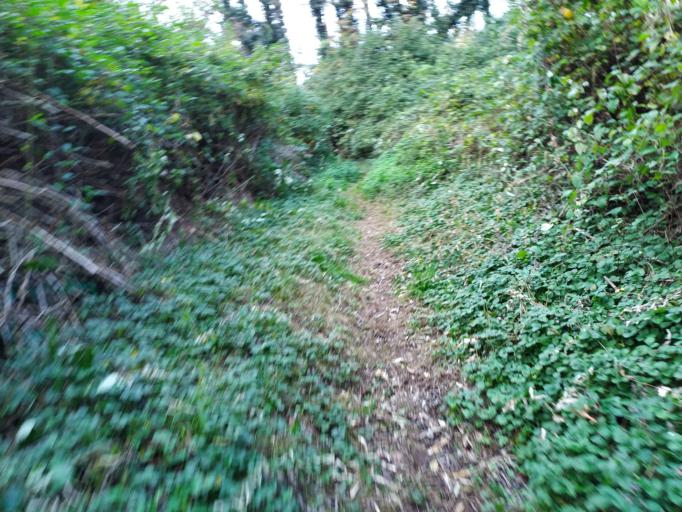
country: IT
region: Veneto
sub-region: Provincia di Vicenza
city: Monte di Malo
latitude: 45.6863
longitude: 11.3602
